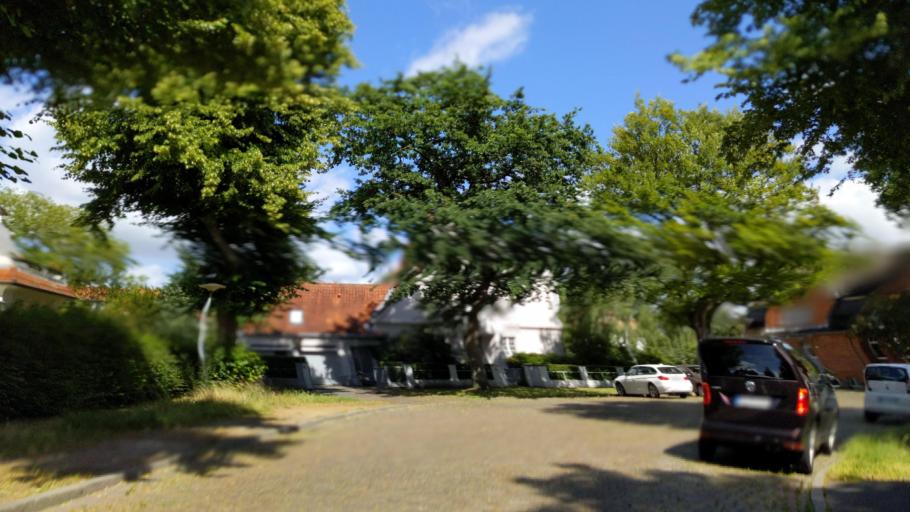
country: DE
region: Schleswig-Holstein
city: Luebeck
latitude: 53.8815
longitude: 10.7037
